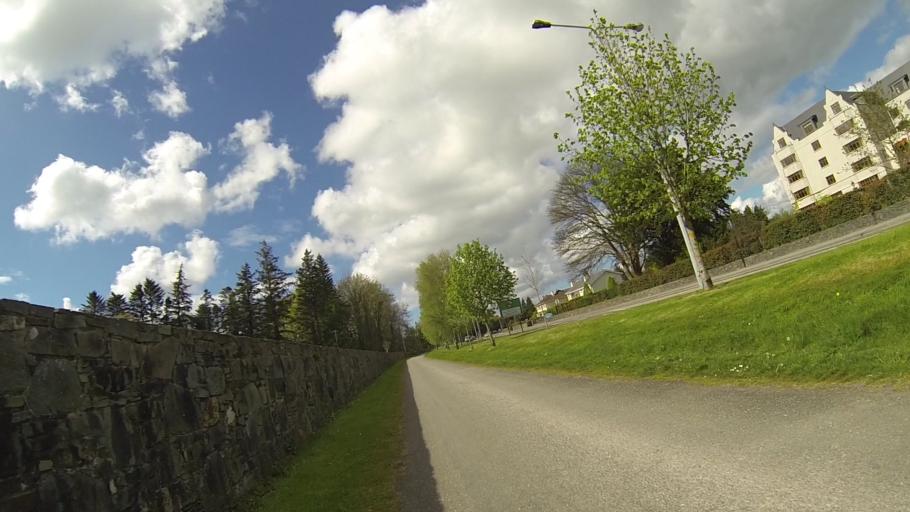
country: IE
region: Munster
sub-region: Ciarrai
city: Cill Airne
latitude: 52.0457
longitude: -9.5052
